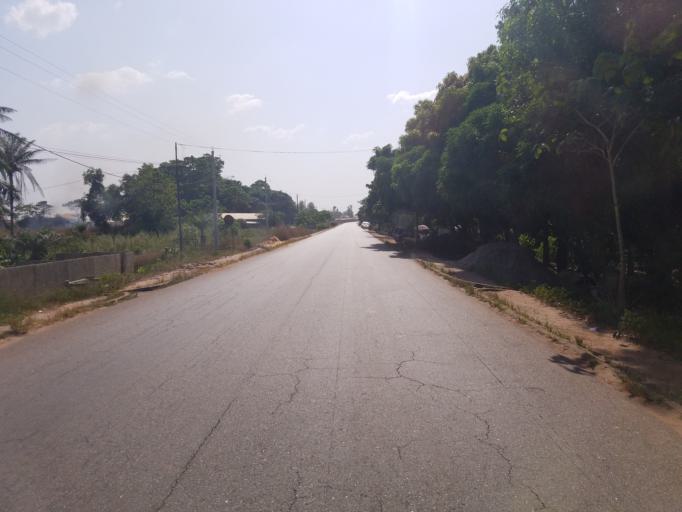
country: GN
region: Boke
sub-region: Fria
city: Fria
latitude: 10.0784
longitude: -13.7003
